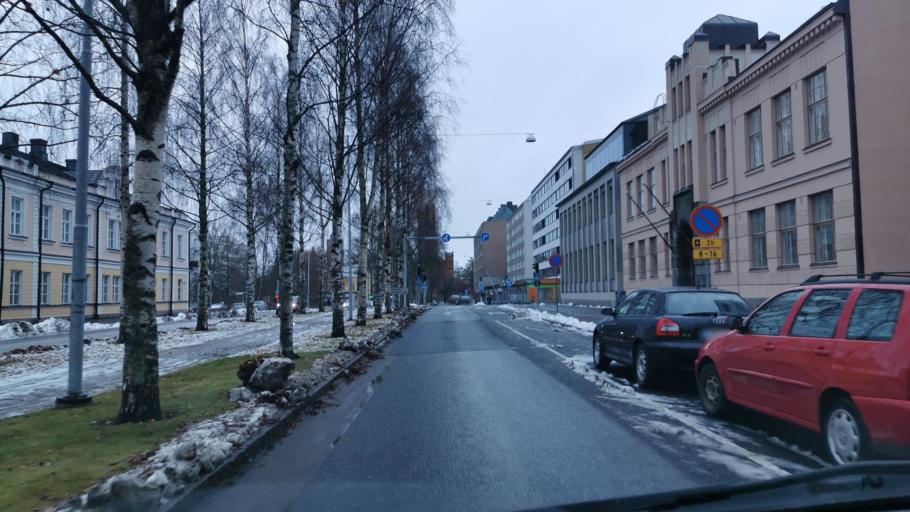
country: FI
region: Ostrobothnia
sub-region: Vaasa
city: Vaasa
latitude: 63.0976
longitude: 21.6075
